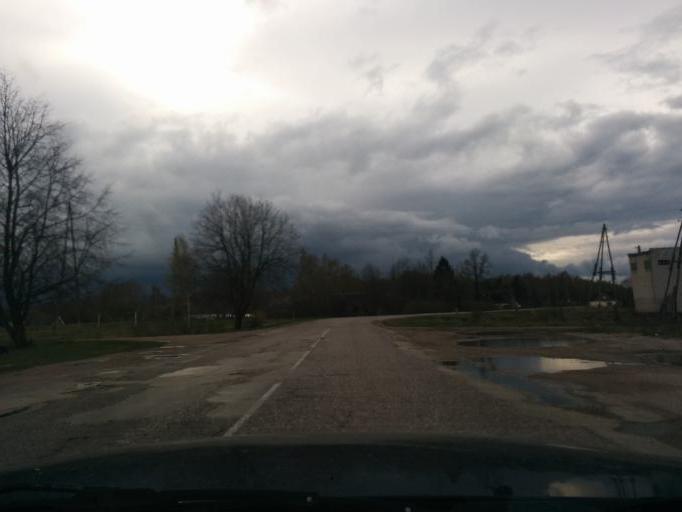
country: LT
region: Siauliu apskritis
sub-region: Joniskis
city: Joniskis
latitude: 56.4185
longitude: 23.5651
